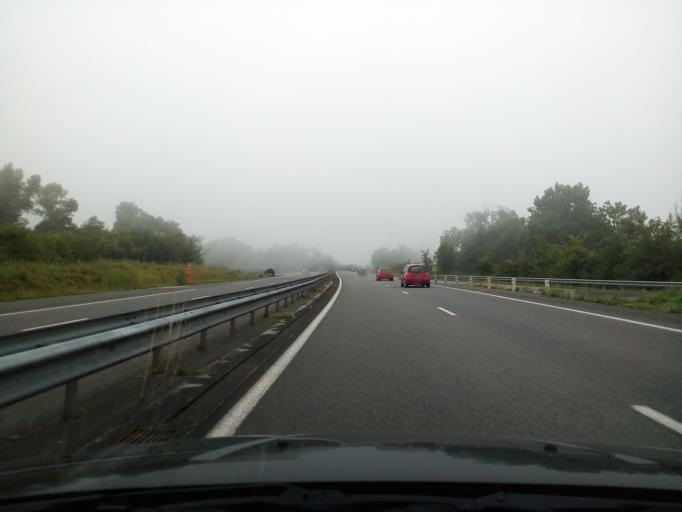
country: FR
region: Poitou-Charentes
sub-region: Departement de la Charente
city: Jarnac
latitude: 45.6911
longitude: -0.1369
